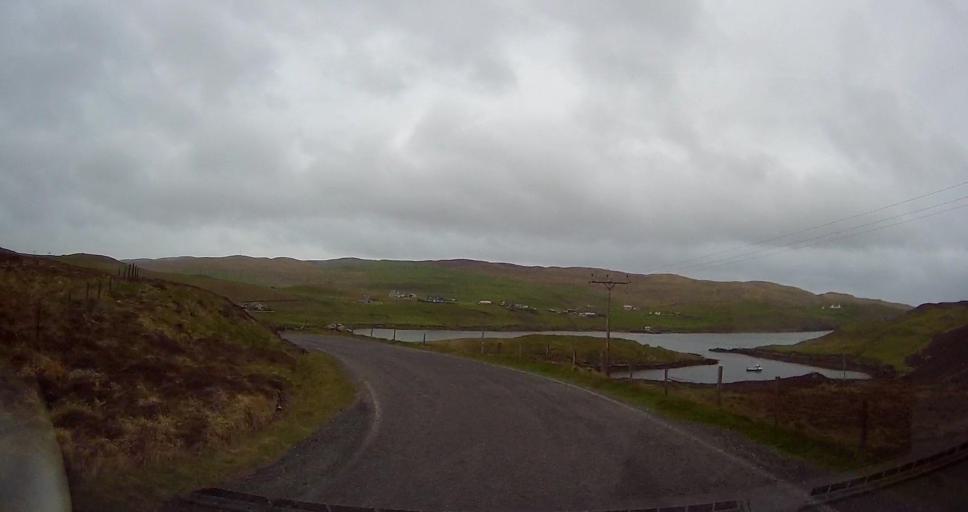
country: GB
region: Scotland
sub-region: Shetland Islands
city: Lerwick
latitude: 60.3794
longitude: -1.3825
